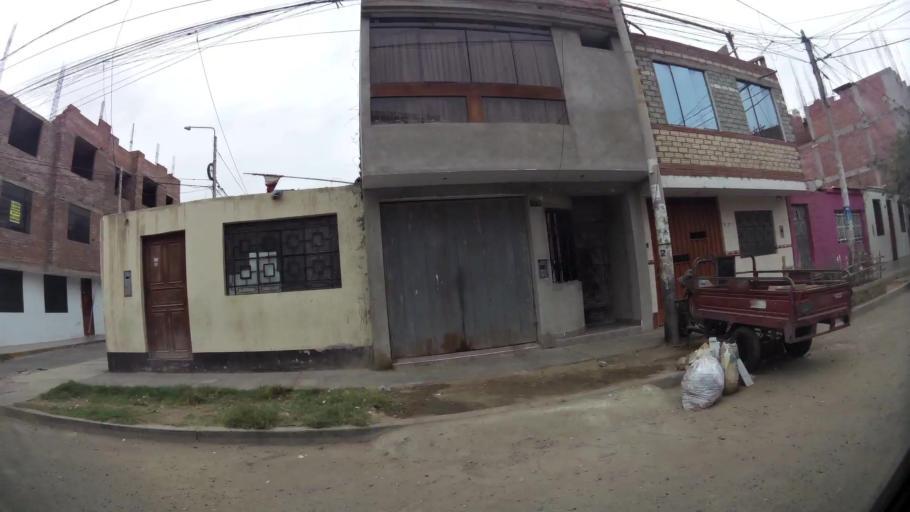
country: PE
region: La Libertad
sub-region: Provincia de Trujillo
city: Trujillo
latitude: -8.1216
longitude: -79.0266
